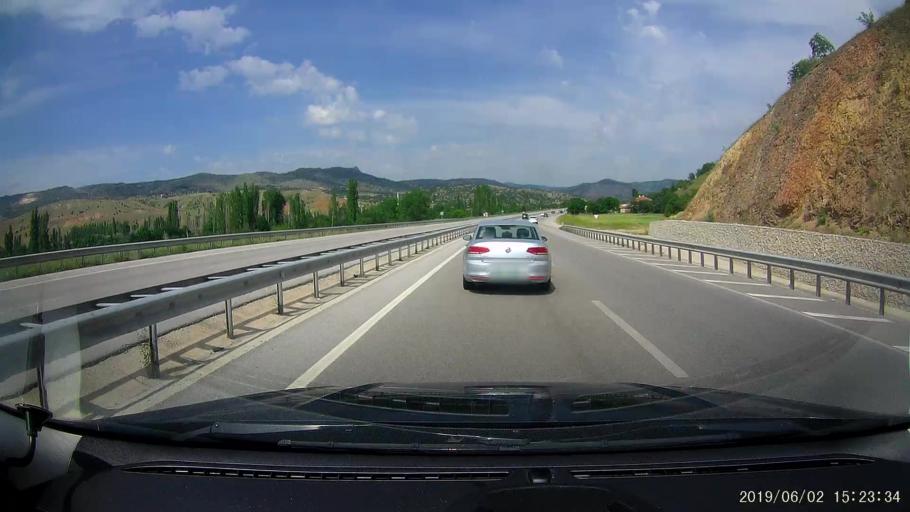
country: TR
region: Amasya
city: Saraycik
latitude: 40.9916
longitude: 34.9831
